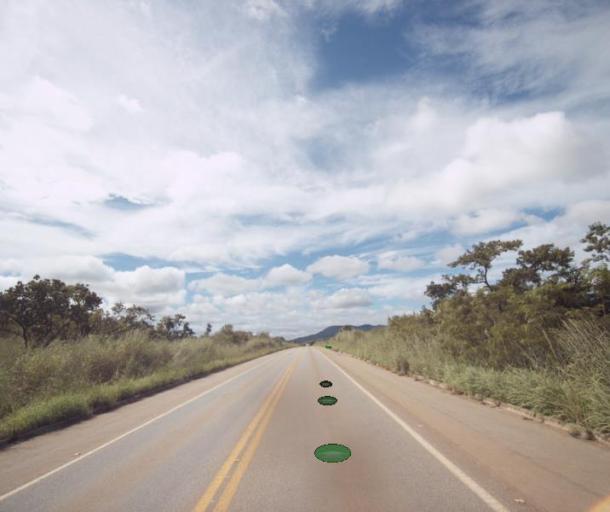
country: BR
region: Goias
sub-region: Barro Alto
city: Barro Alto
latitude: -15.1788
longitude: -48.7908
